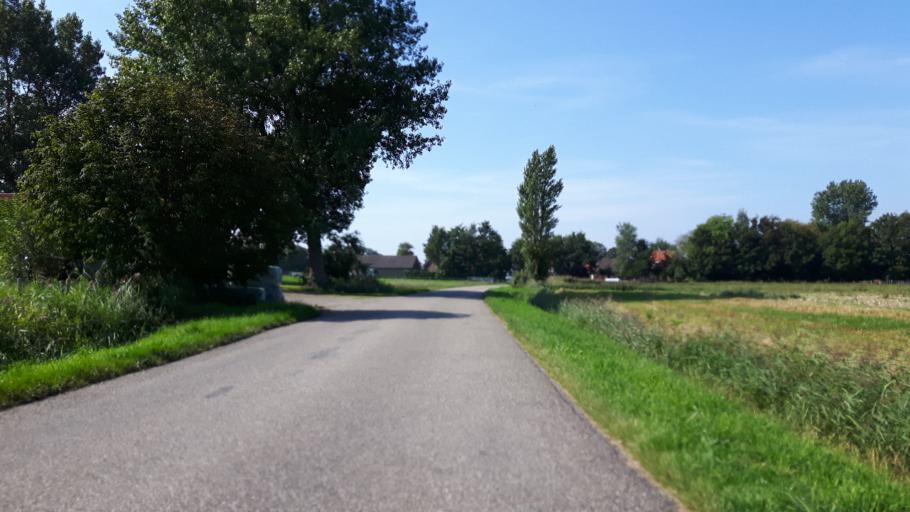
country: NL
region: Friesland
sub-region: Gemeente Dongeradeel
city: Holwerd
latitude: 53.3544
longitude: 5.8656
